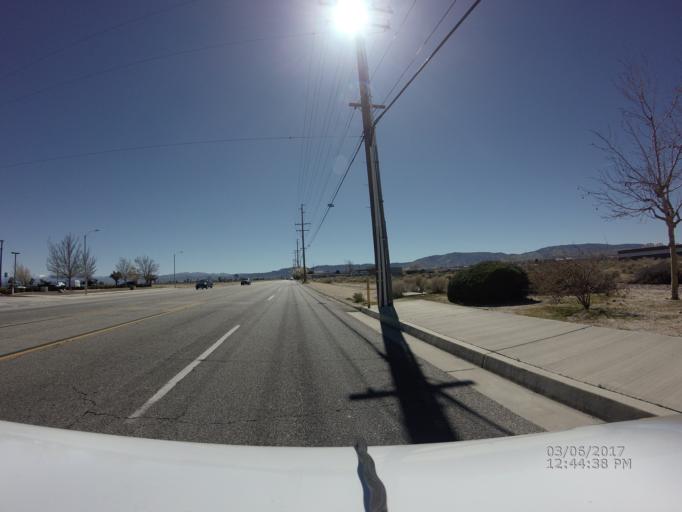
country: US
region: California
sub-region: Los Angeles County
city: Desert View Highlands
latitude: 34.6374
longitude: -118.1479
